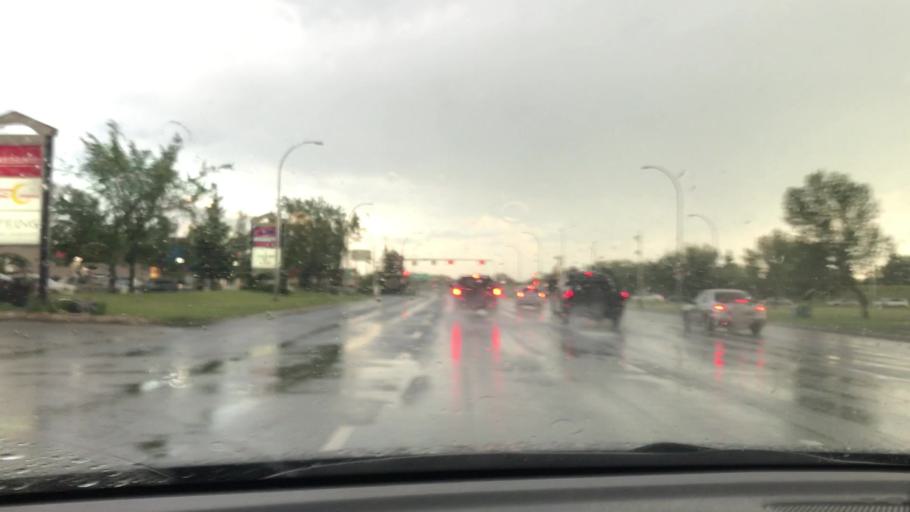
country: CA
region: Alberta
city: Edmonton
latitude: 53.4689
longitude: -113.4957
